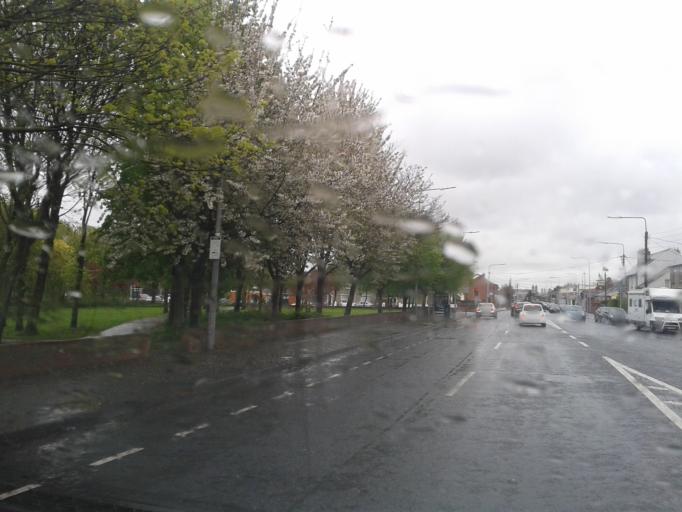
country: IE
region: Leinster
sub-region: South Dublin
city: Terenure
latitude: 53.3130
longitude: -6.2983
